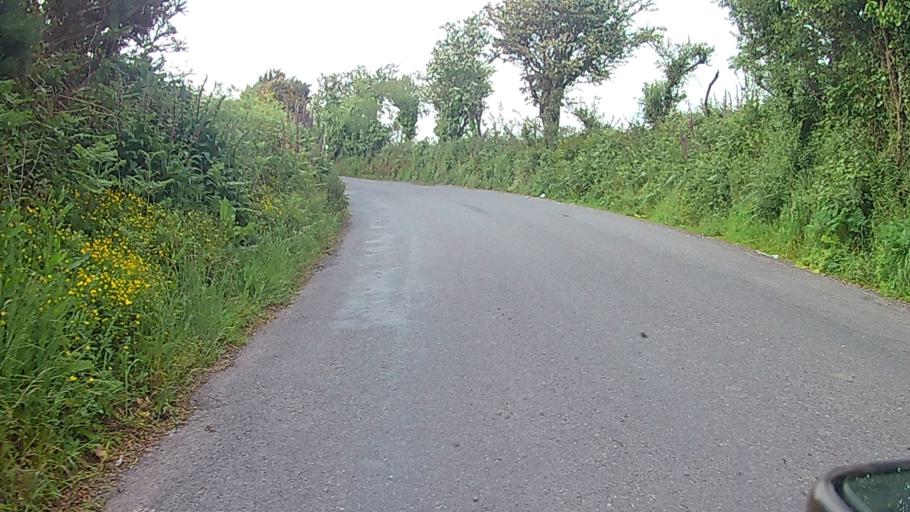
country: IE
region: Munster
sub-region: County Cork
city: Watergrasshill
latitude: 51.9679
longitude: -8.4106
